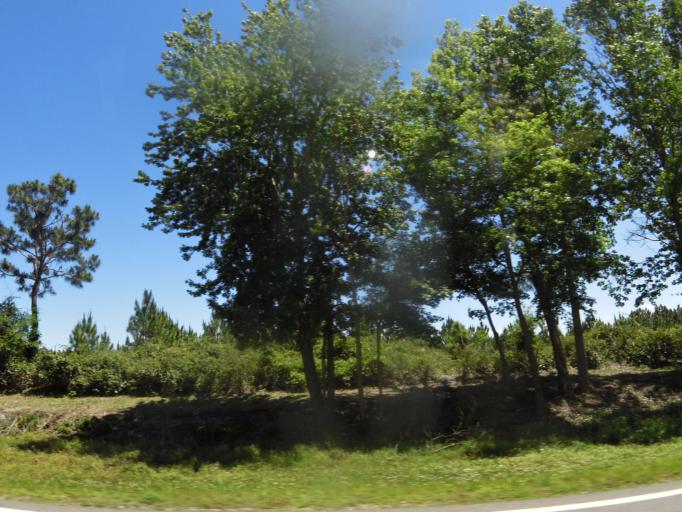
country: US
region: Florida
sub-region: Saint Johns County
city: Fruit Cove
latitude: 30.0357
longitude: -81.5864
